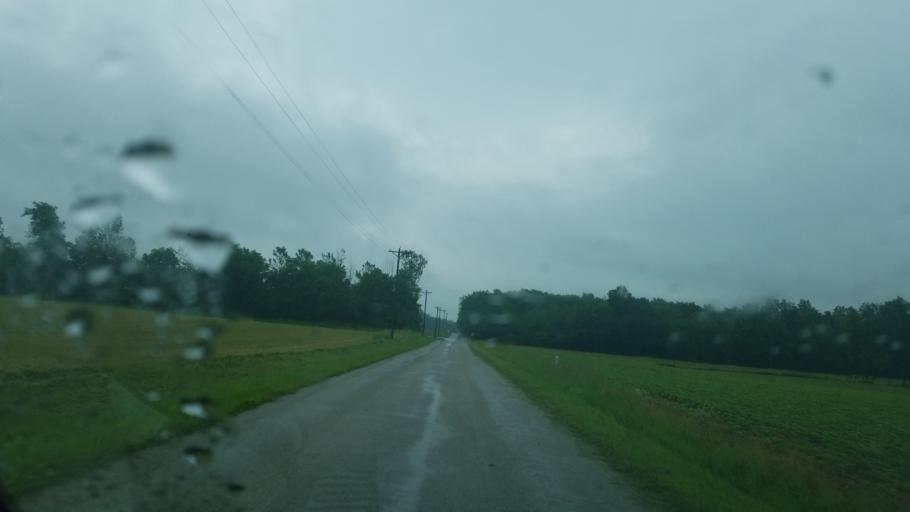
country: US
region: Ohio
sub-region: Huron County
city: Plymouth
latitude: 40.9451
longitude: -82.7261
